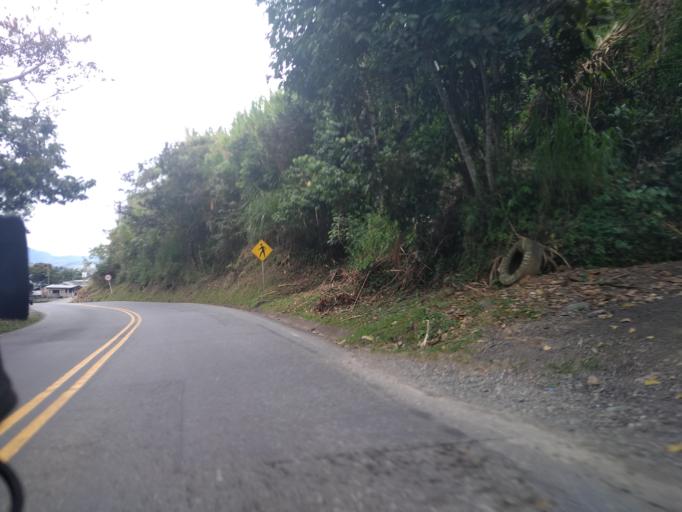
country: CO
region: Cauca
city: Rosas
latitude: 2.2485
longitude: -76.7679
